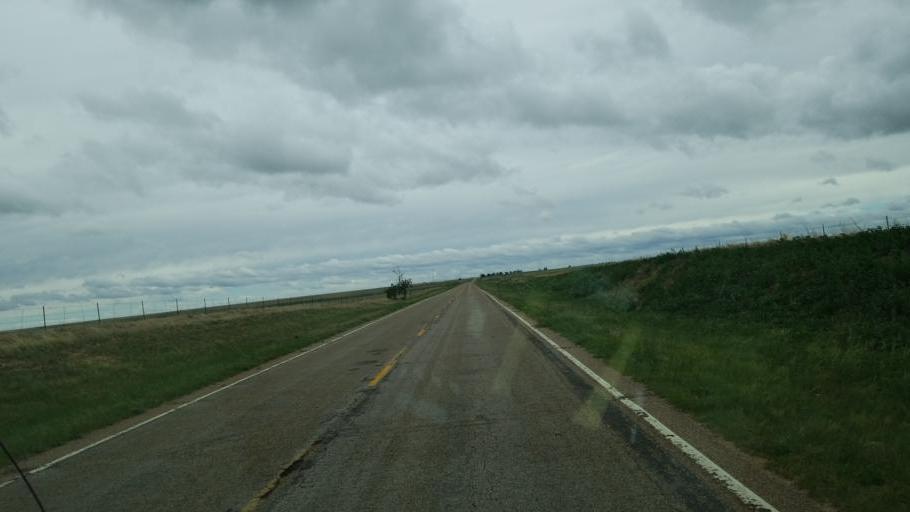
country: US
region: Colorado
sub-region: Lincoln County
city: Hugo
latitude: 38.8518
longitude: -103.6759
